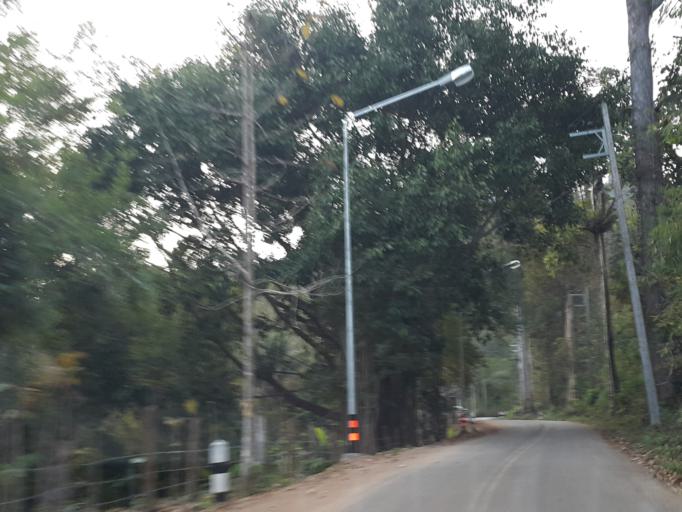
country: TH
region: Lampang
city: Mueang Pan
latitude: 18.8203
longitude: 99.4549
